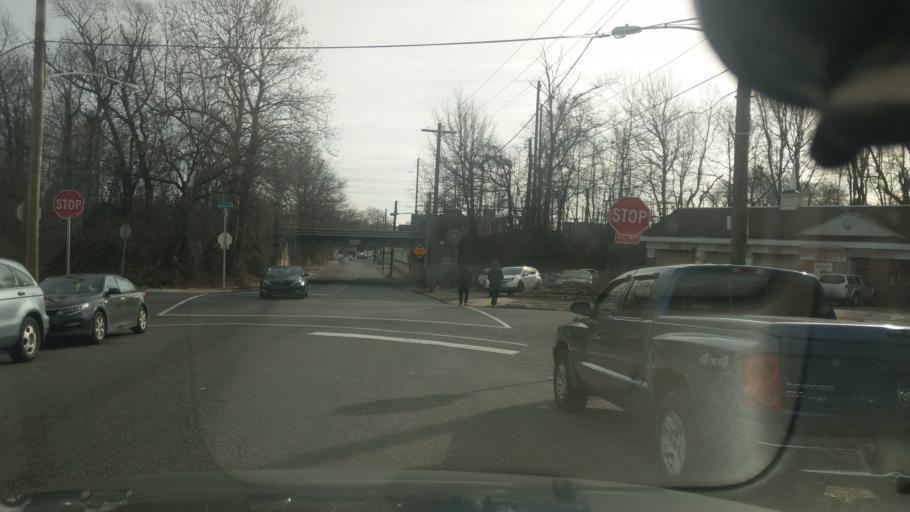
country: US
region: Pennsylvania
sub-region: Montgomery County
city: Wyncote
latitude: 40.0367
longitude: -75.1376
